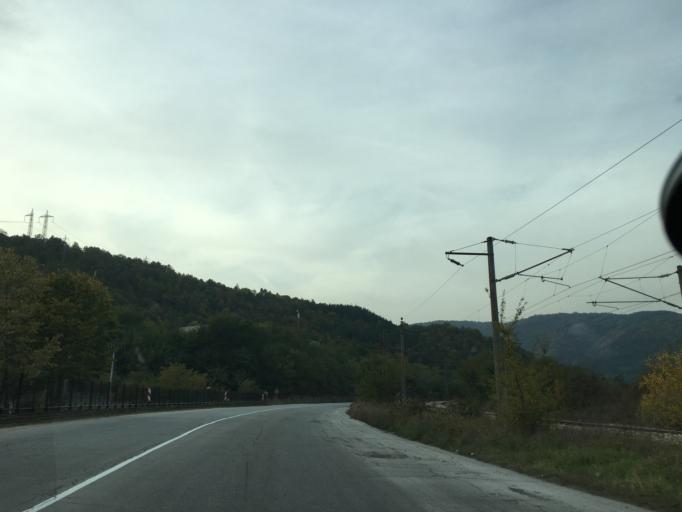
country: BG
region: Pazardzhik
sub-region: Obshtina Belovo
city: Belovo
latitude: 42.2323
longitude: 23.9496
